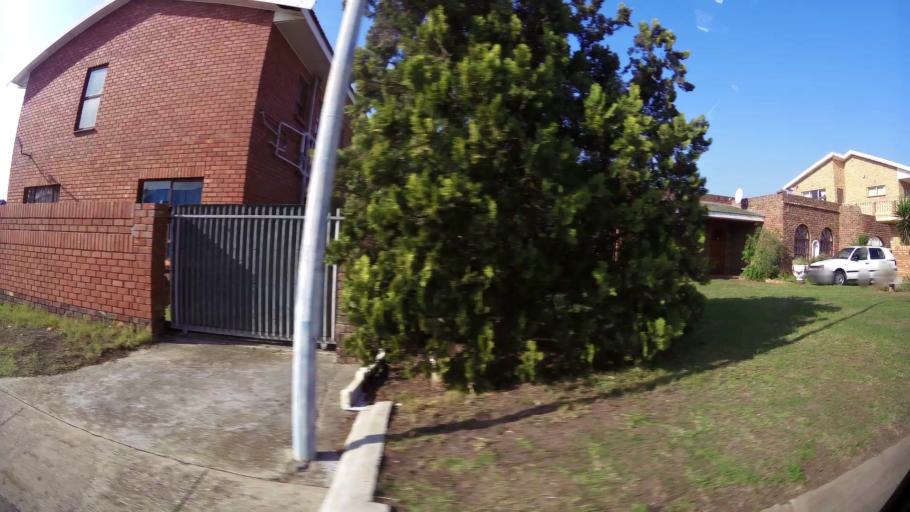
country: ZA
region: Eastern Cape
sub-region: Nelson Mandela Bay Metropolitan Municipality
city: Port Elizabeth
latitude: -33.9209
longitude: 25.5300
